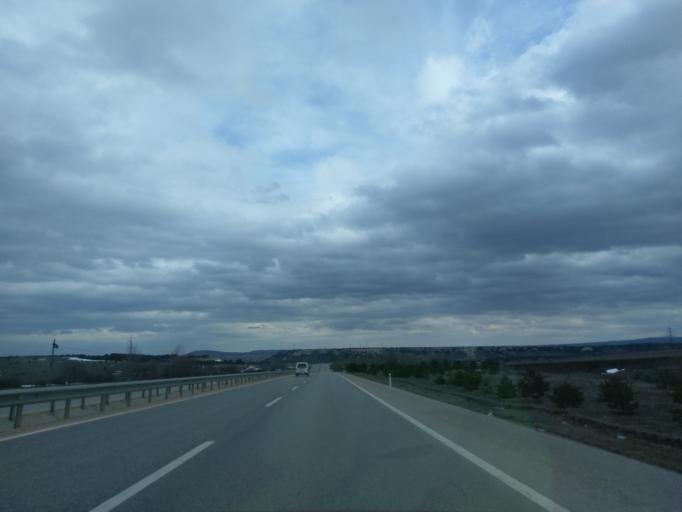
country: TR
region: Eskisehir
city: Inonu
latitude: 39.7253
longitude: 30.3225
